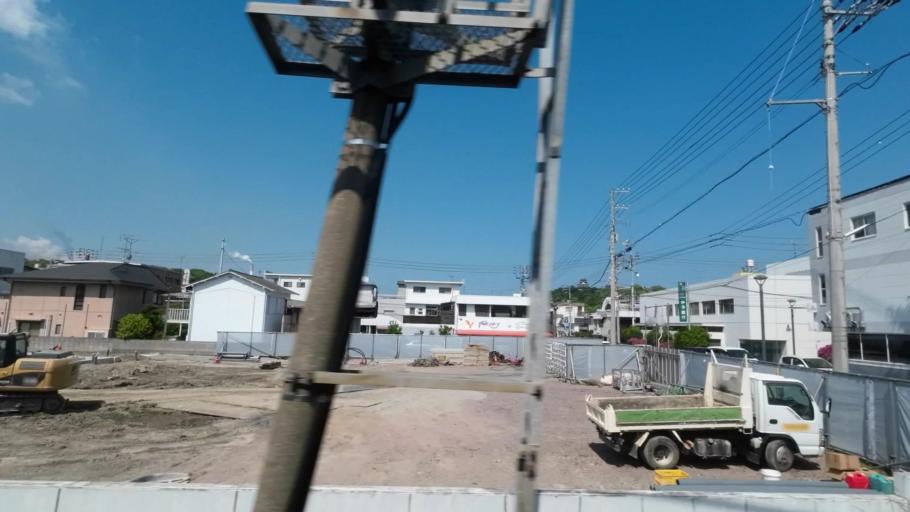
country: JP
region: Ehime
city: Kawanoecho
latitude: 34.0111
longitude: 133.5754
